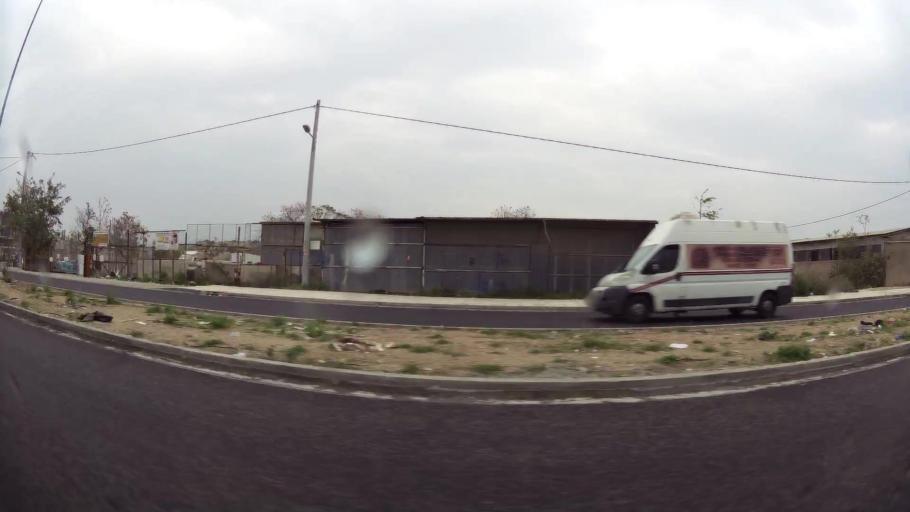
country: GR
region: Attica
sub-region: Nomarchia Athinas
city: Aigaleo
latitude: 37.9836
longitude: 23.6916
